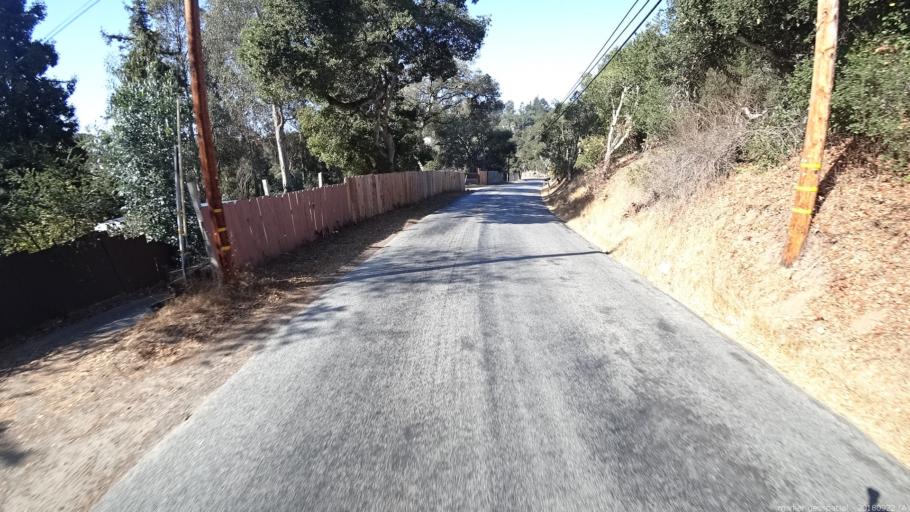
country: US
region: California
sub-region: Monterey County
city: Prunedale
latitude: 36.8090
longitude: -121.6475
